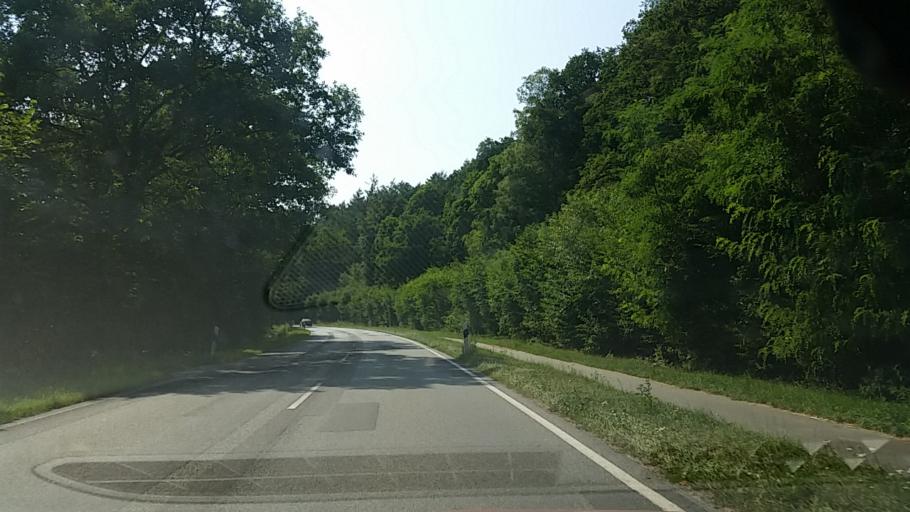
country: DE
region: Schleswig-Holstein
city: Trittau
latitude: 53.6071
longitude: 10.4277
